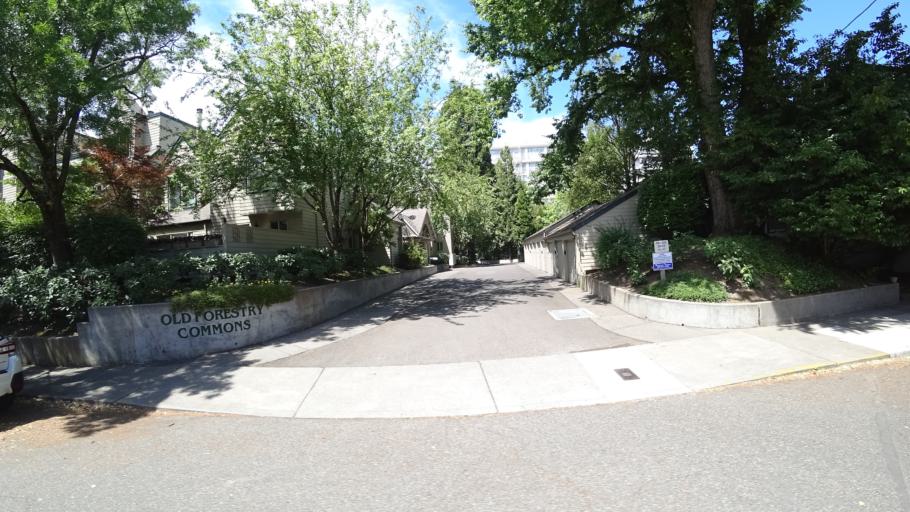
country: US
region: Oregon
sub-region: Multnomah County
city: Portland
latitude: 45.5360
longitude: -122.7080
